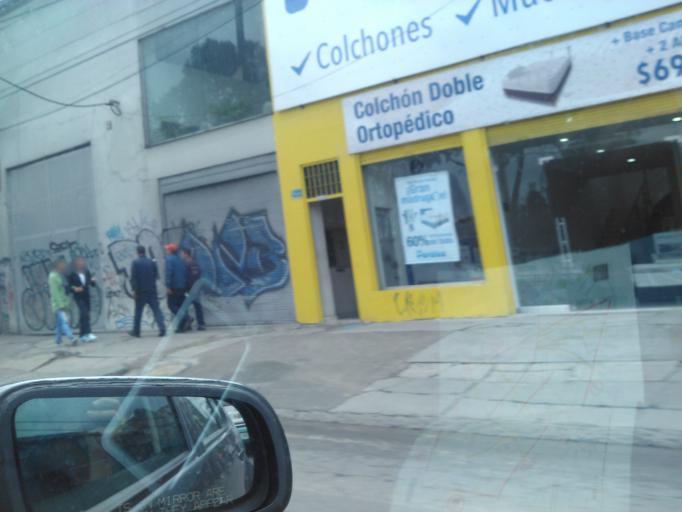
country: CO
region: Bogota D.C.
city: Bogota
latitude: 4.6259
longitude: -74.1235
